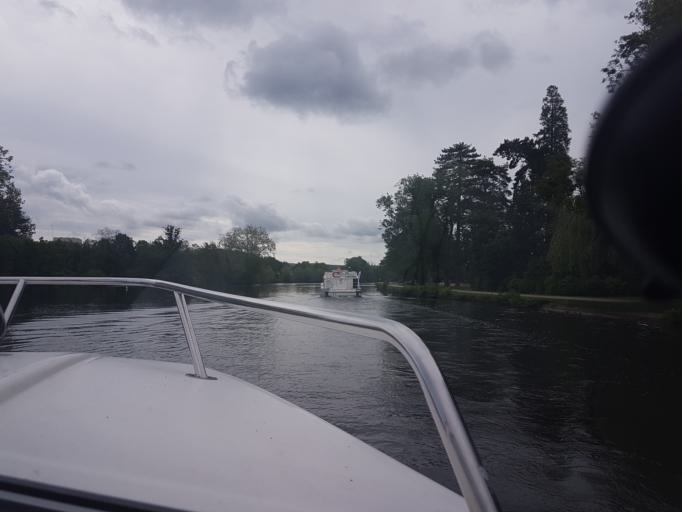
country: FR
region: Bourgogne
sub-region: Departement de l'Yonne
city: Auxerre
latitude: 47.7926
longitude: 3.5845
